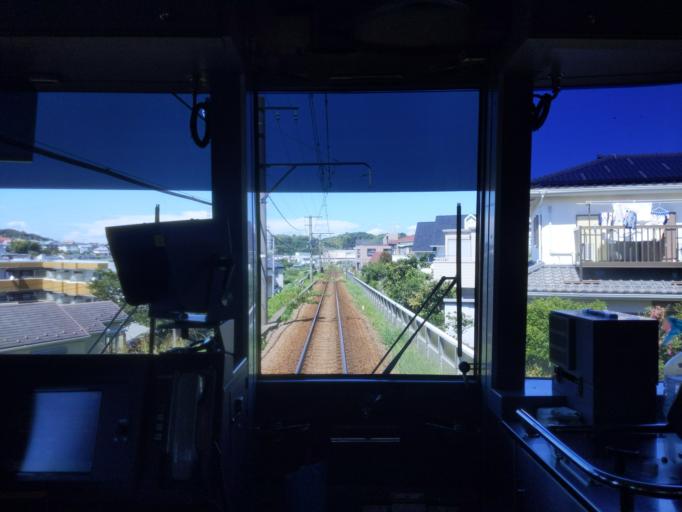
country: JP
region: Tokyo
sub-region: Machida-shi
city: Machida
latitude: 35.5371
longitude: 139.4924
